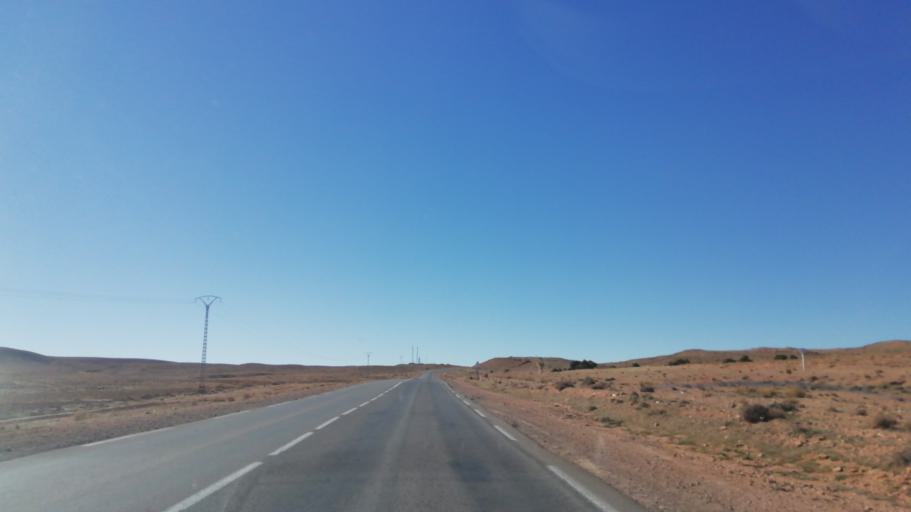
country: DZ
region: El Bayadh
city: El Bayadh
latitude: 33.6693
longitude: 1.4394
